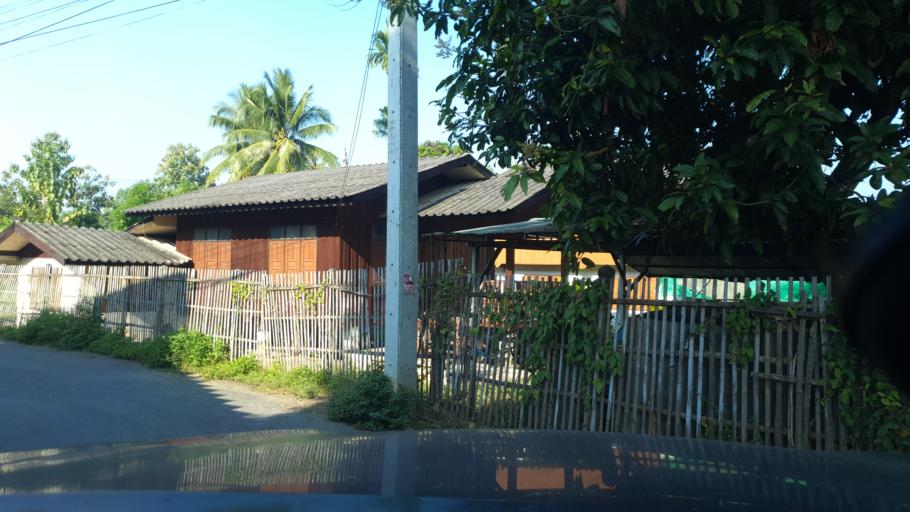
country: TH
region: Chiang Mai
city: San Kamphaeng
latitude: 18.7520
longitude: 99.1455
